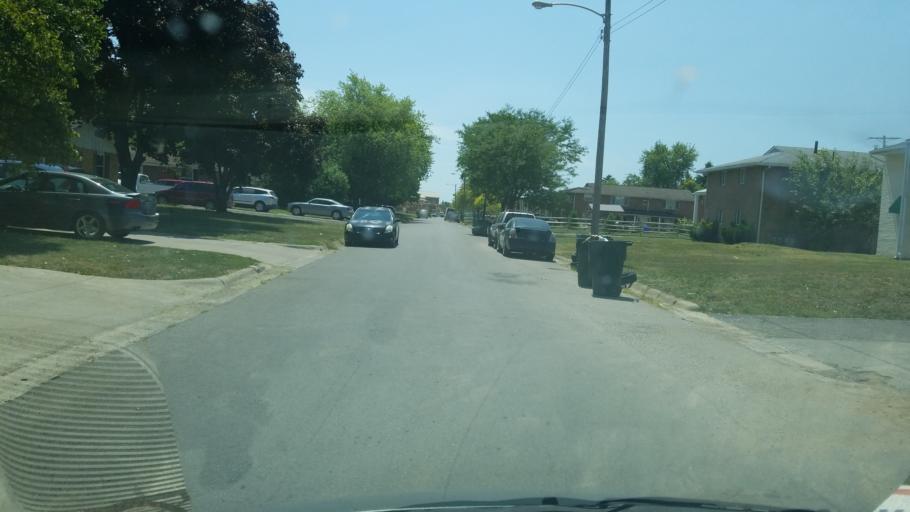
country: US
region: Ohio
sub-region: Franklin County
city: Lincoln Village
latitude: 39.9369
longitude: -83.0952
